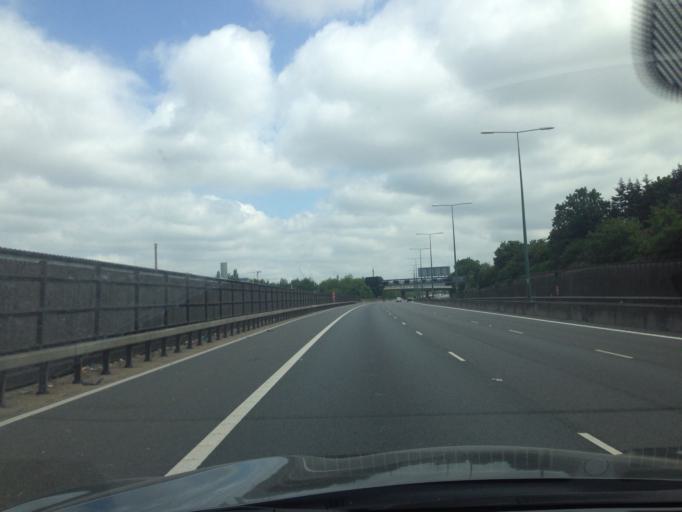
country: GB
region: England
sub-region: Greater London
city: Hendon
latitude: 51.5839
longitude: -0.2388
